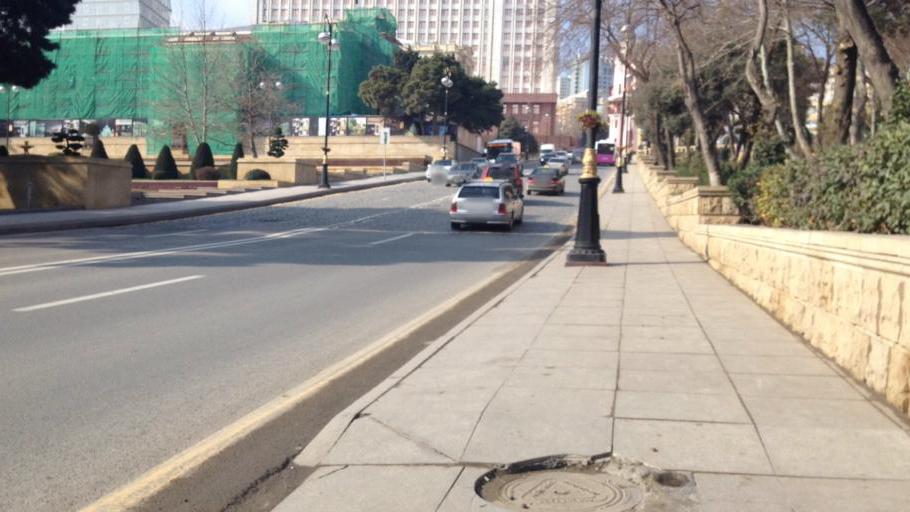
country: AZ
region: Baki
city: Badamdar
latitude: 40.3632
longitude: 49.8332
